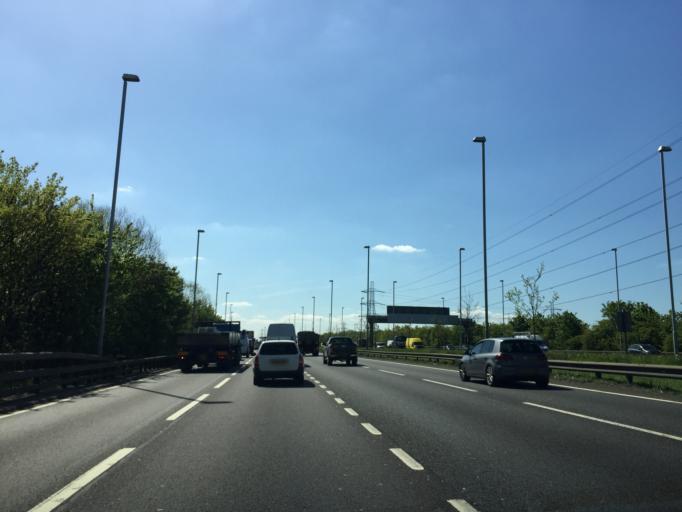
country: GB
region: England
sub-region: Greater London
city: Woodford Green
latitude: 51.5816
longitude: 0.0407
